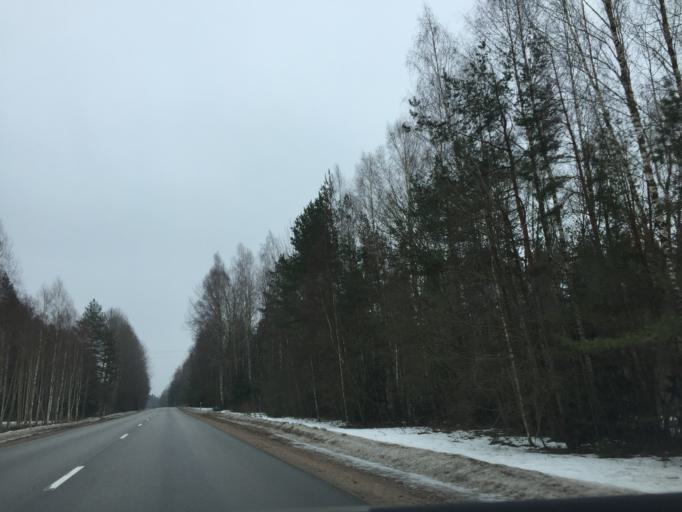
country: LV
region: Lecava
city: Iecava
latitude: 56.6117
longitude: 24.0315
